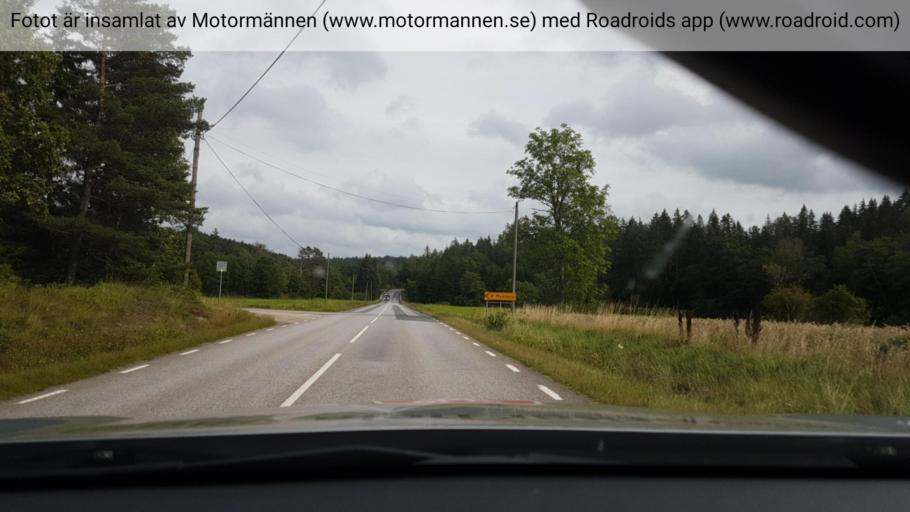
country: SE
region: Vaestra Goetaland
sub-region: Sotenas Kommun
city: Hunnebostrand
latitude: 58.5636
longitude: 11.3877
